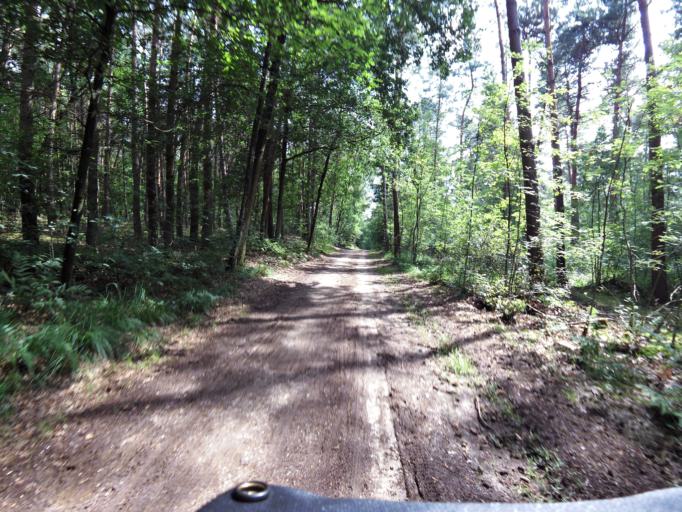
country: NL
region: Limburg
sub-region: Gemeente Roerdalen
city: Vlodrop
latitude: 51.1575
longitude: 6.1054
